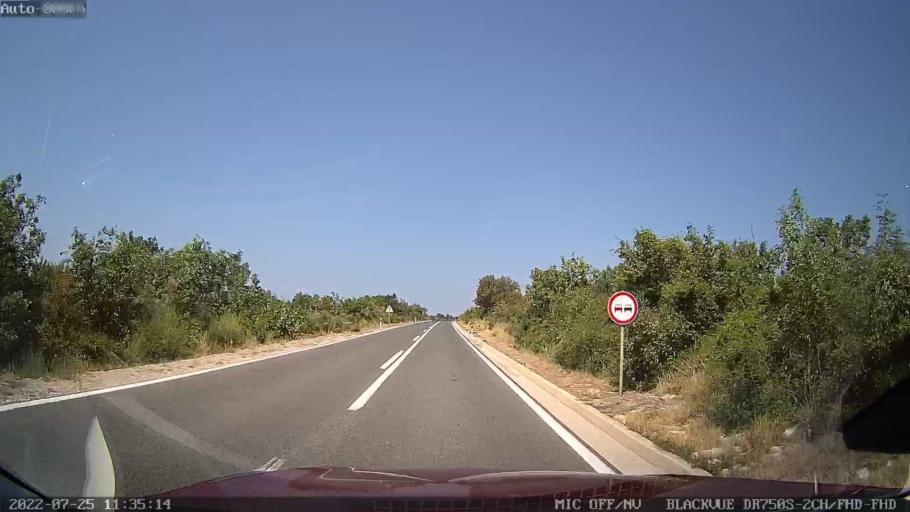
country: HR
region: Zadarska
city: Policnik
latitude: 44.2327
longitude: 15.4116
